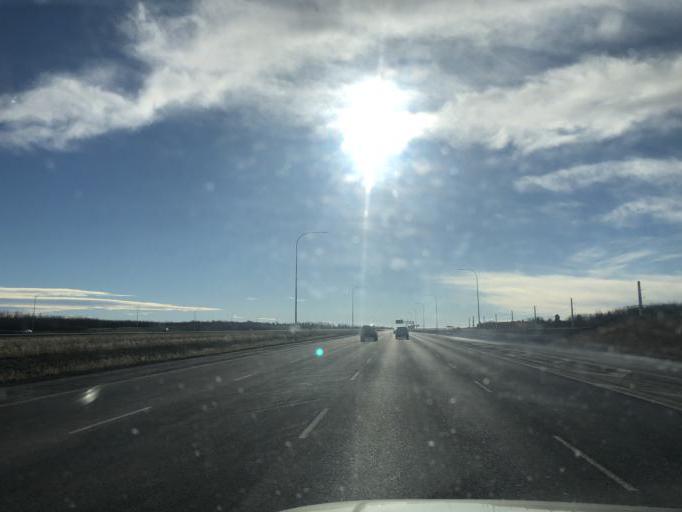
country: CA
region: Alberta
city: Calgary
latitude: 50.9701
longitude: -114.1527
